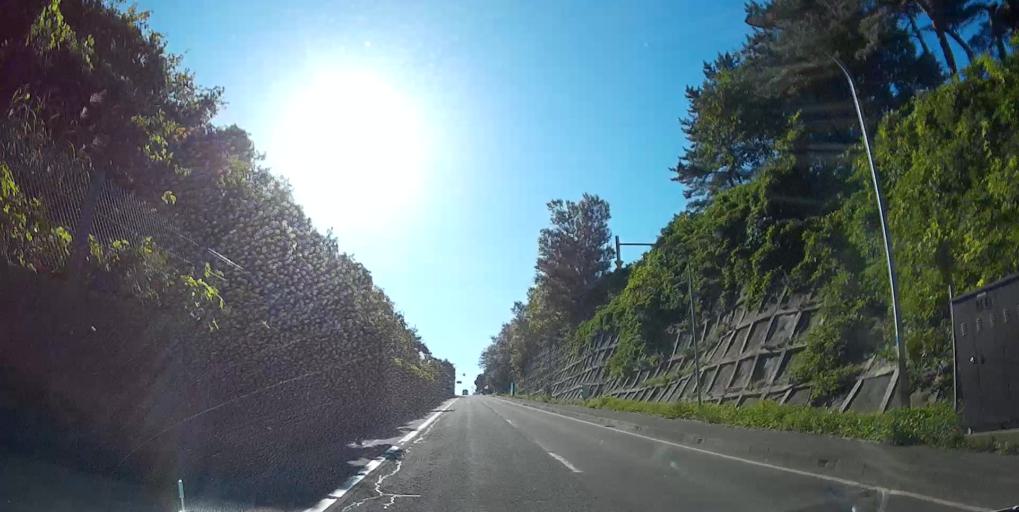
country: JP
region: Hokkaido
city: Kamiiso
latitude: 42.2250
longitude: 139.8248
